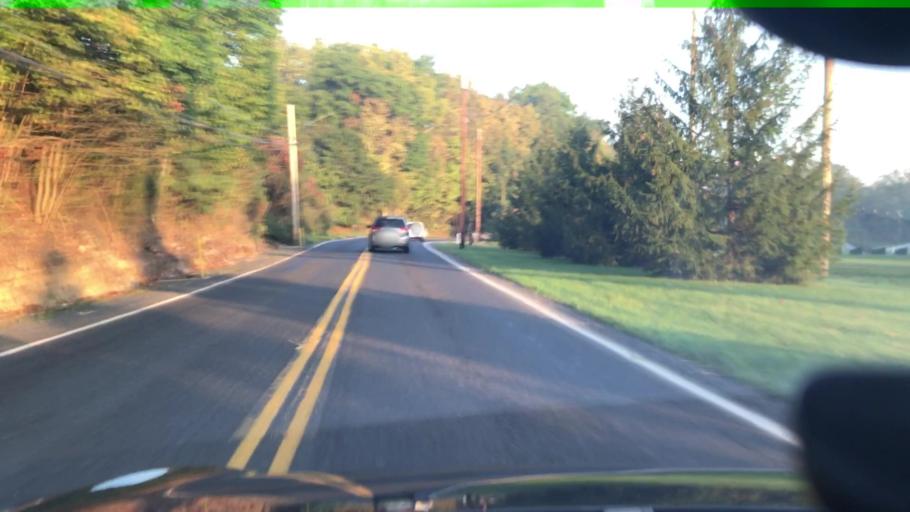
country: US
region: Pennsylvania
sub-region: Cumberland County
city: Lower Allen
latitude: 40.1747
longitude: -76.9226
